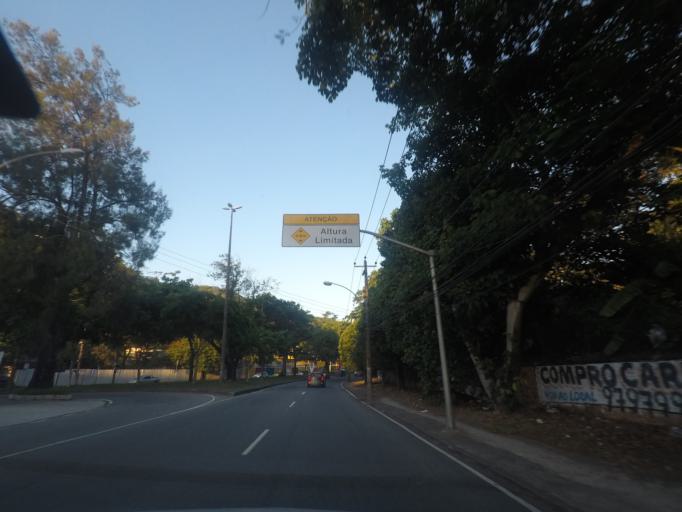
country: BR
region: Rio de Janeiro
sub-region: Rio De Janeiro
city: Rio de Janeiro
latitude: -22.9311
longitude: -43.3250
